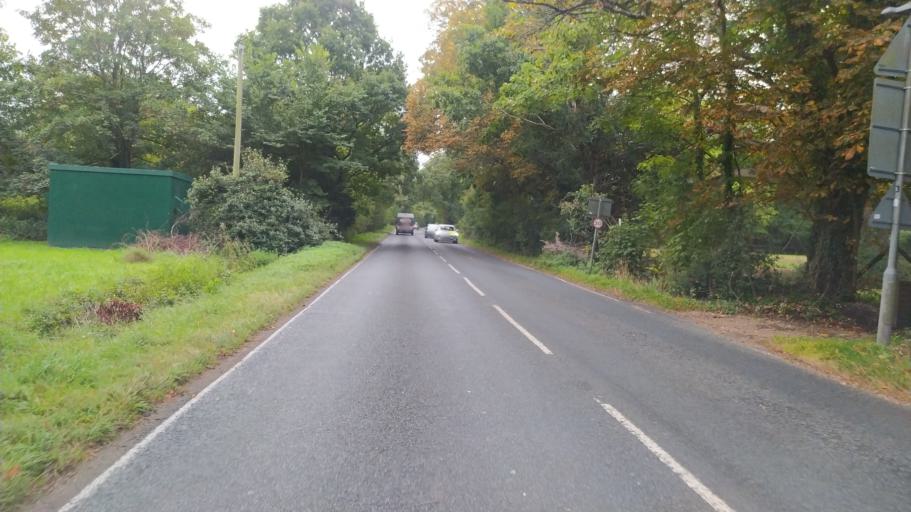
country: GB
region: England
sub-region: Hampshire
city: Brockenhurst
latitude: 50.8164
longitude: -1.5719
